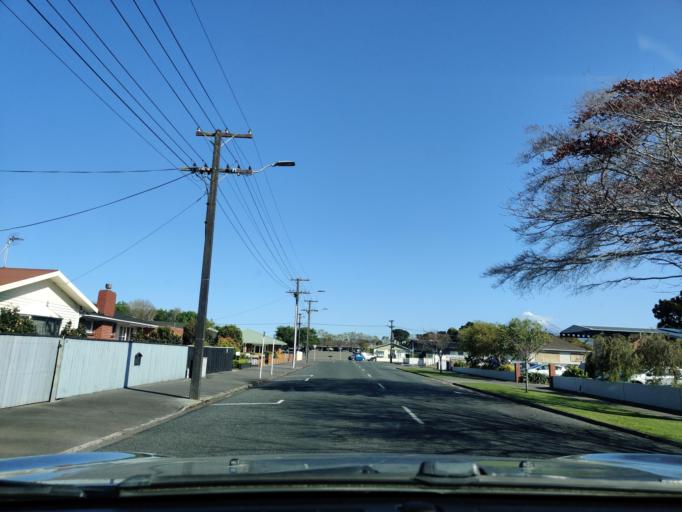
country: NZ
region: Taranaki
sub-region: New Plymouth District
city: New Plymouth
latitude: -39.0730
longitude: 174.0583
